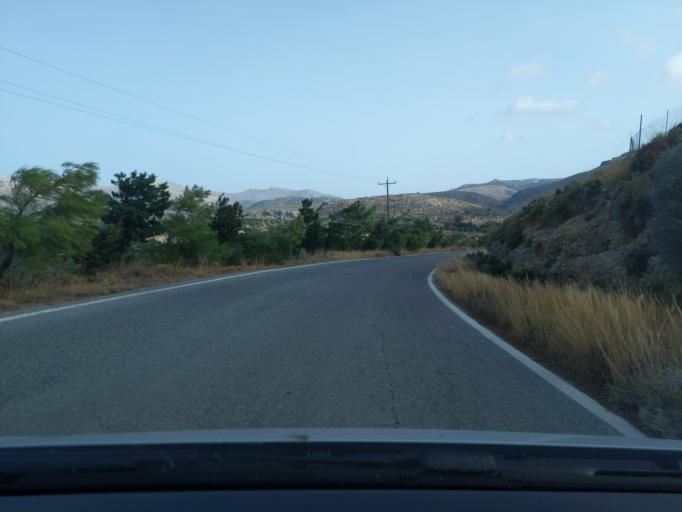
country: GR
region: Crete
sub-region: Nomos Lasithiou
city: Palekastro
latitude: 35.0944
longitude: 26.2343
